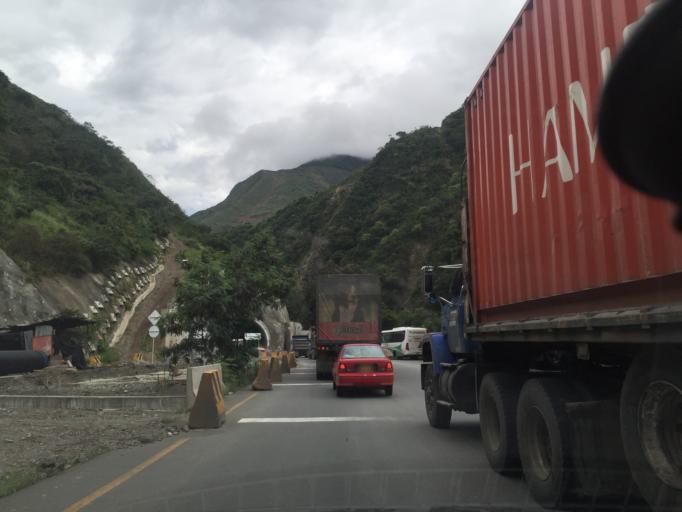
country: CO
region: Valle del Cauca
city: Dagua
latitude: 3.7802
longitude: -76.7133
